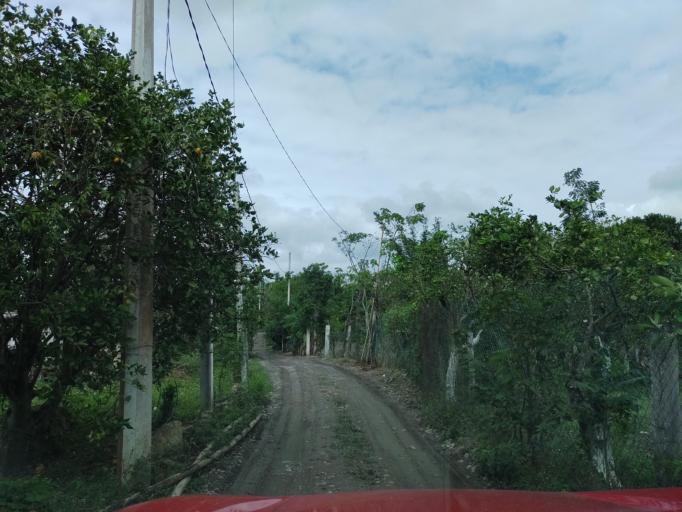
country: MX
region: Veracruz
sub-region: Papantla
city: El Chote
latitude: 20.4365
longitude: -97.3766
